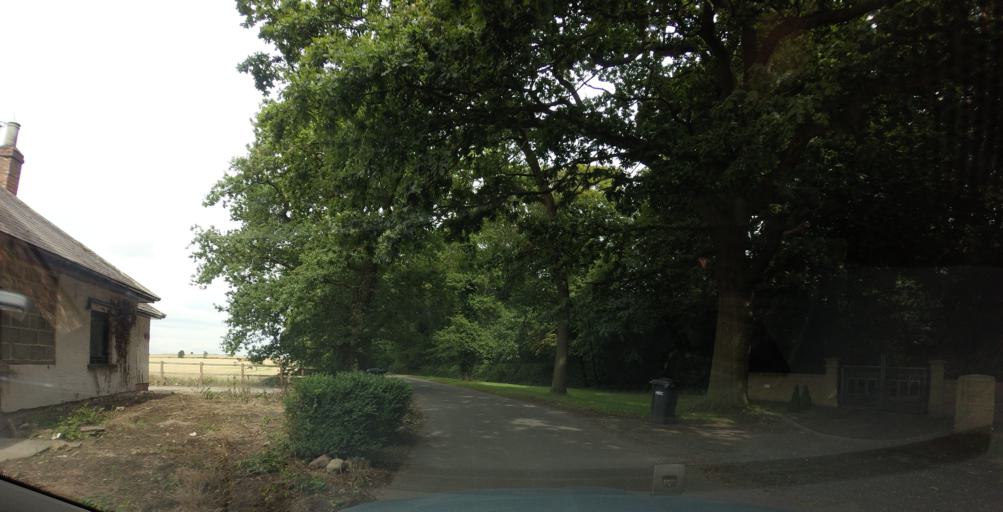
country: GB
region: England
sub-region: North Yorkshire
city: Ripon
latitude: 54.1390
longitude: -1.4764
